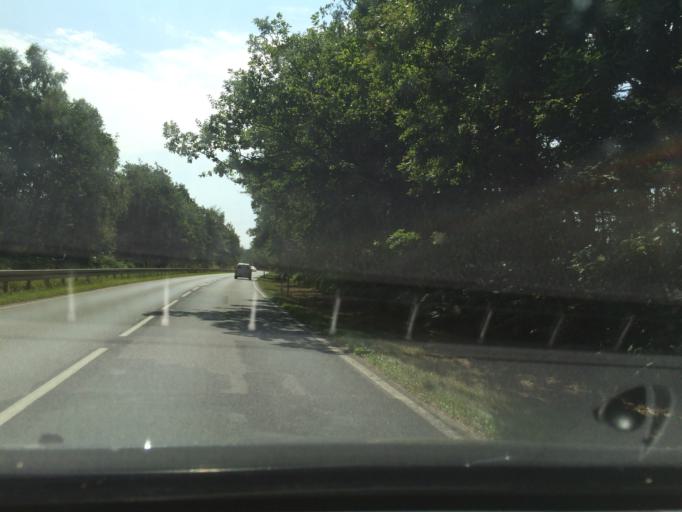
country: DE
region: Mecklenburg-Vorpommern
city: Ostseebad Binz
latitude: 54.4090
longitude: 13.5957
